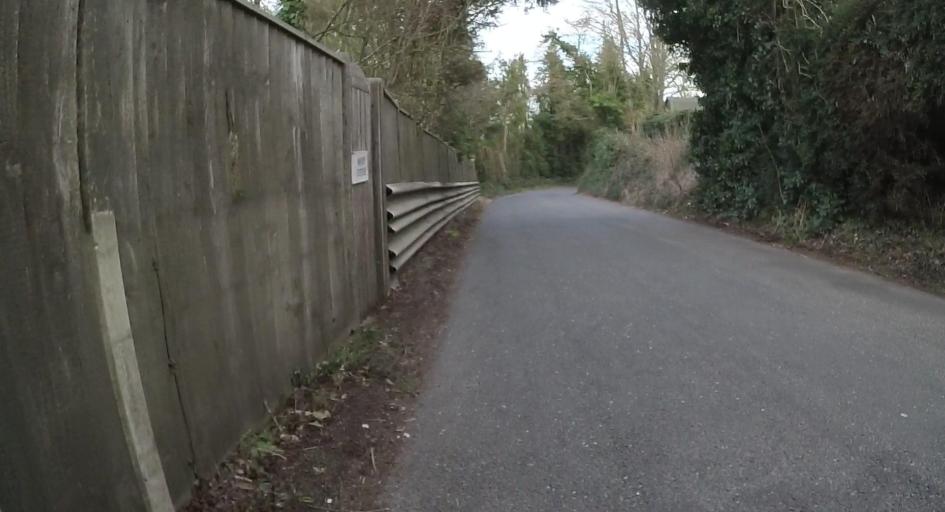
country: GB
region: England
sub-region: Hampshire
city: Andover
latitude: 51.1533
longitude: -1.4473
